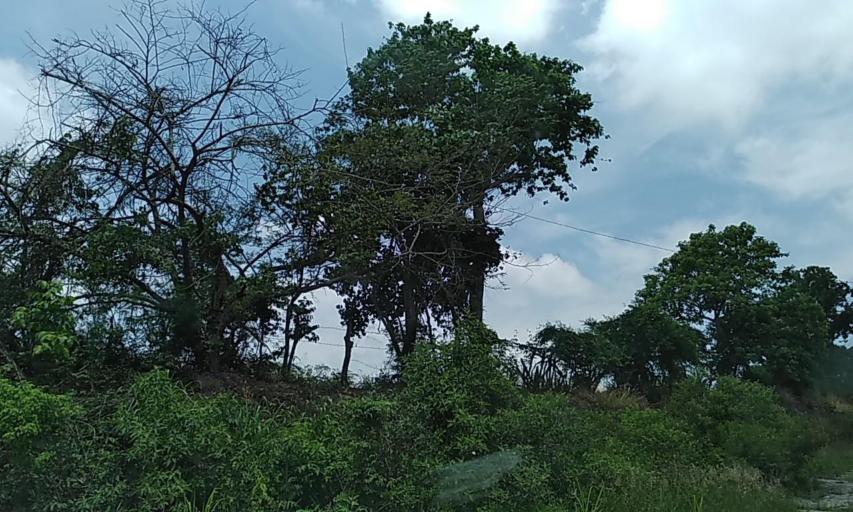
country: MX
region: Veracruz
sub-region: Emiliano Zapata
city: Dos Rios
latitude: 19.4382
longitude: -96.7483
